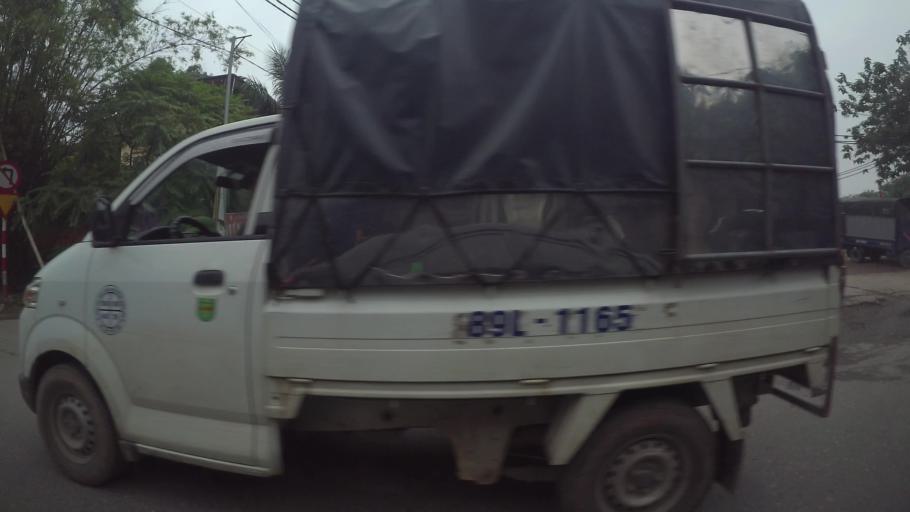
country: VN
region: Ha Noi
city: Hai BaTrung
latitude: 20.9797
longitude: 105.8882
